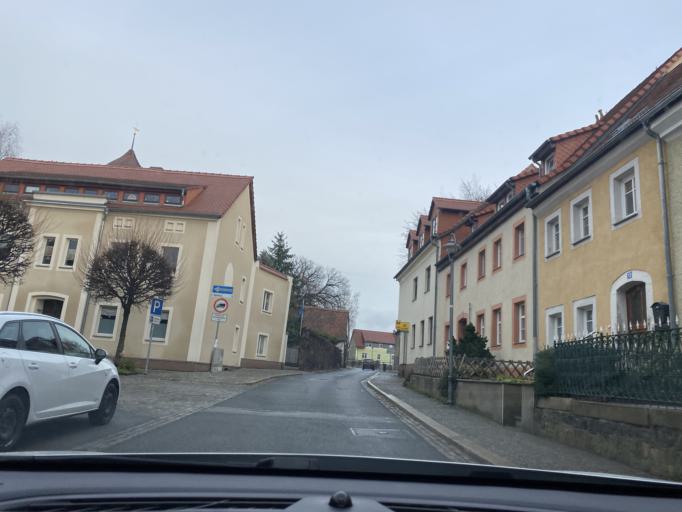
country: DE
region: Saxony
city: Reichenbach
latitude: 51.1408
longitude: 14.8024
